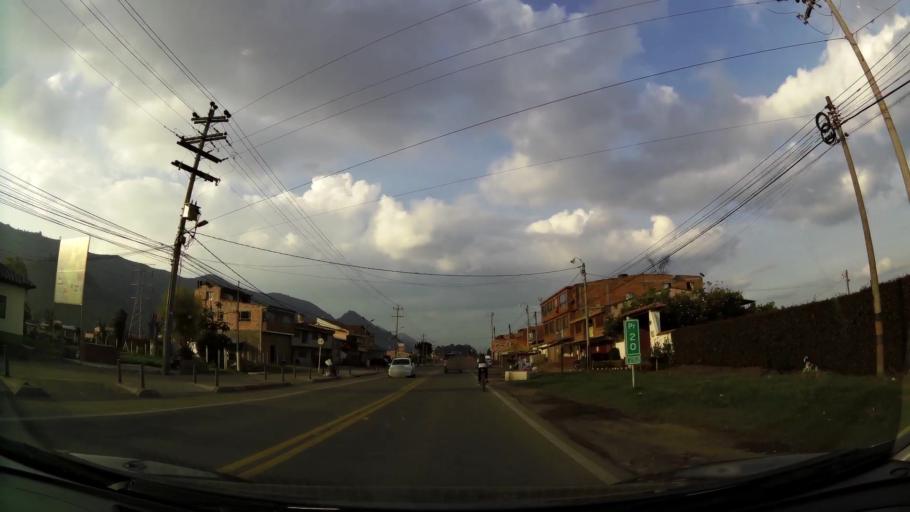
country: CO
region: Cundinamarca
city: Cota
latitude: 4.8208
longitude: -74.0936
